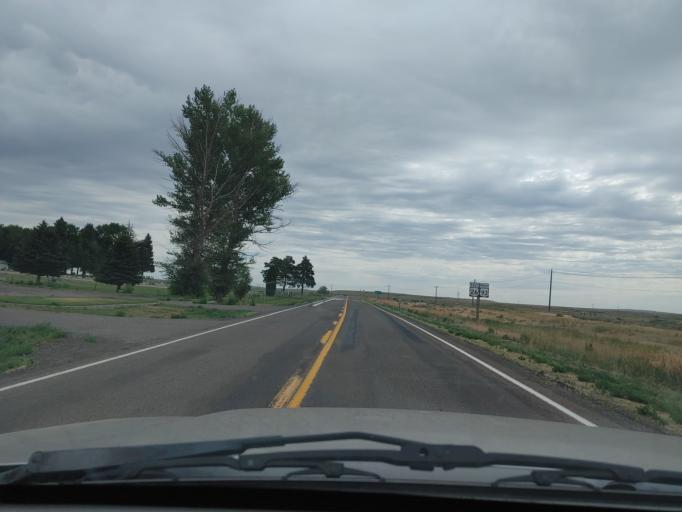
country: US
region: Idaho
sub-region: Lincoln County
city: Shoshone
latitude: 43.0494
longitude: -114.1475
